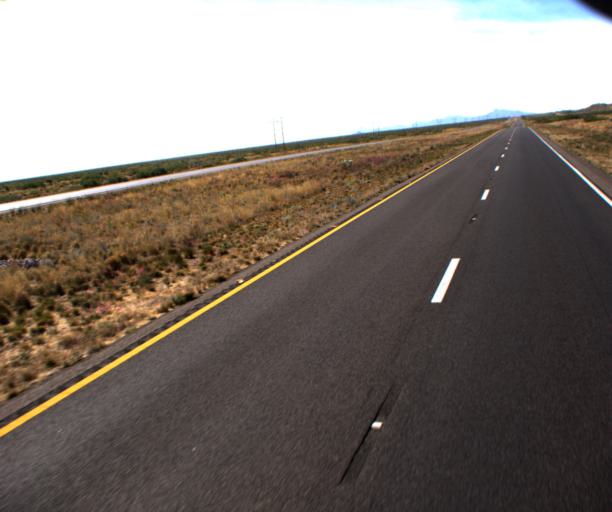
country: US
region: Arizona
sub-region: Graham County
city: Swift Trail Junction
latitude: 32.5619
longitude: -109.6796
